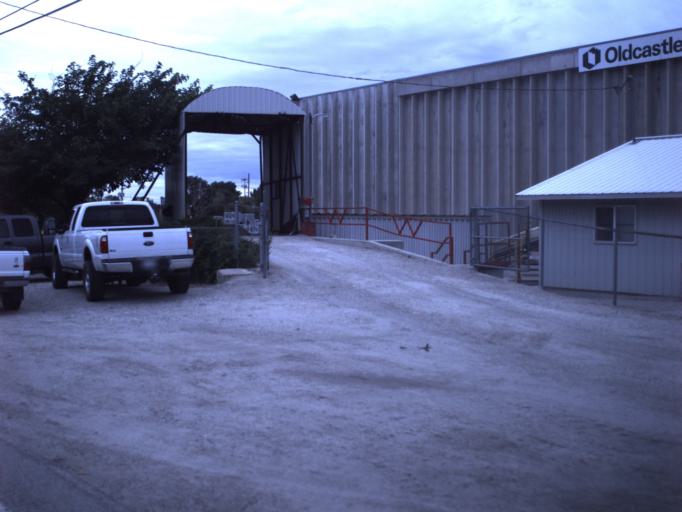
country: US
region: Utah
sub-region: Weber County
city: Ogden
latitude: 41.2397
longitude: -111.9785
